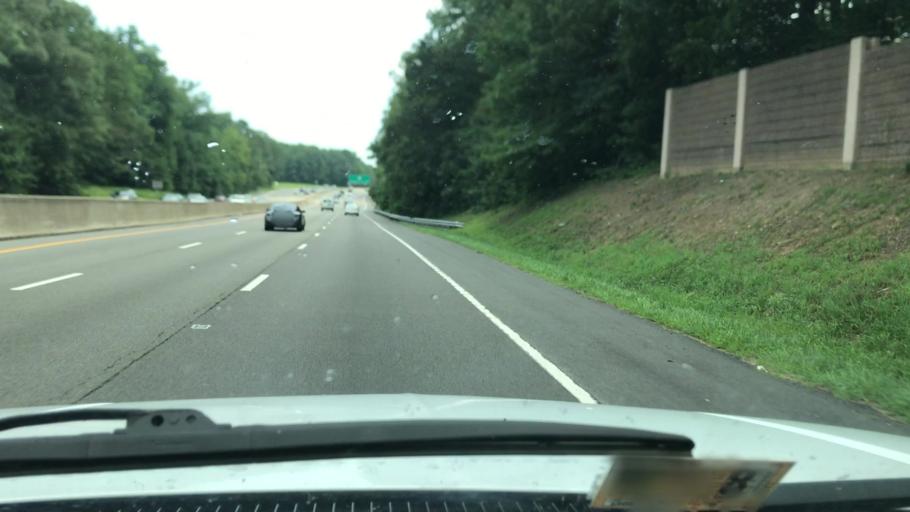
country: US
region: Virginia
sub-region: Chesterfield County
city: Bensley
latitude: 37.4652
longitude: -77.5037
